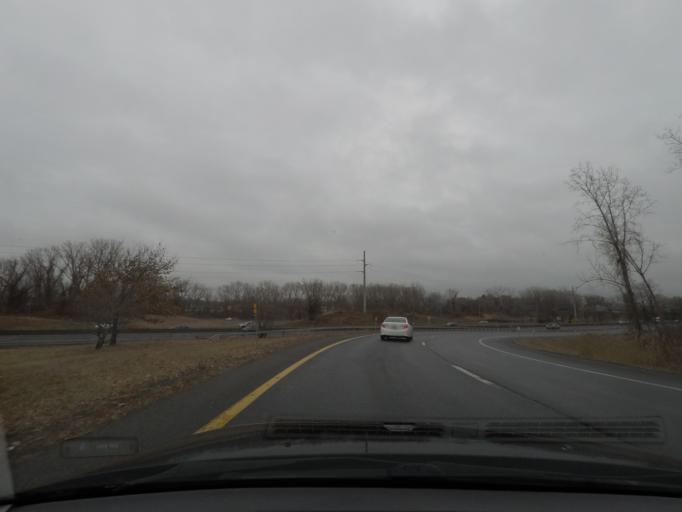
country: US
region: New York
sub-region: Albany County
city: Roessleville
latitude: 42.6915
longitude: -73.8237
